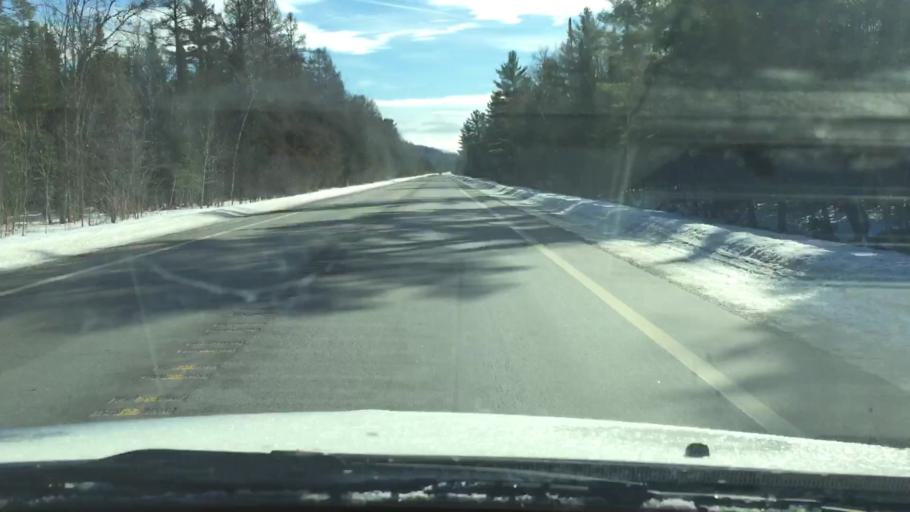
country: US
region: Michigan
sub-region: Antrim County
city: Mancelona
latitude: 45.0262
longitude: -85.0658
